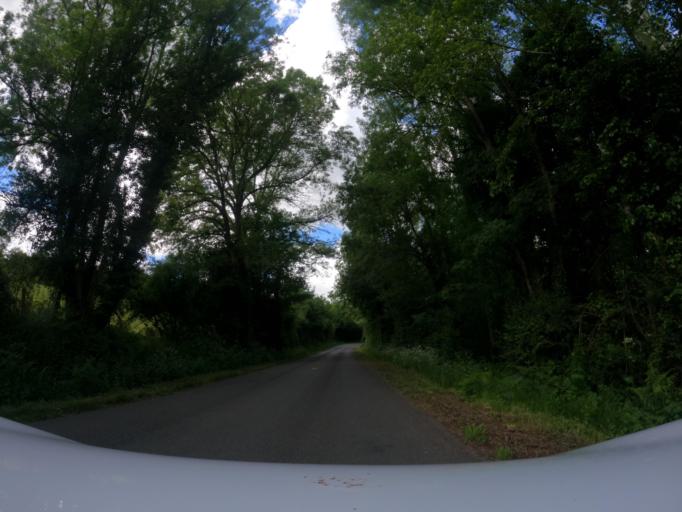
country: FR
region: Pays de la Loire
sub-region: Departement de la Vendee
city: Le Champ-Saint-Pere
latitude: 46.5025
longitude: -1.3509
